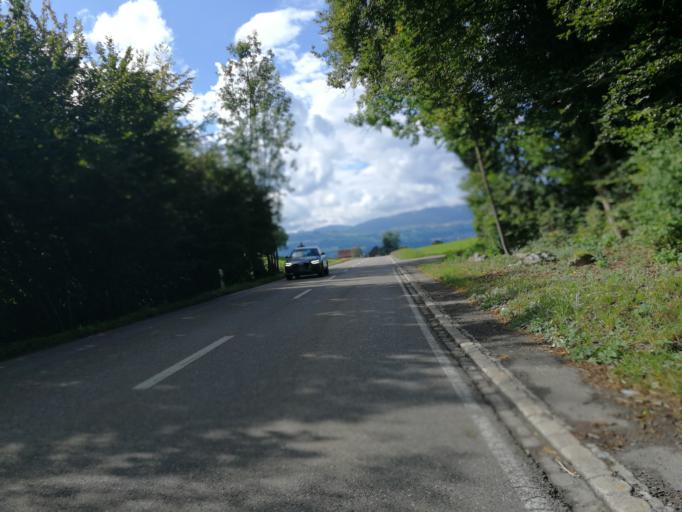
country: CH
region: Zurich
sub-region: Bezirk Meilen
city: Hombrechtikon
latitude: 47.2464
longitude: 8.7688
